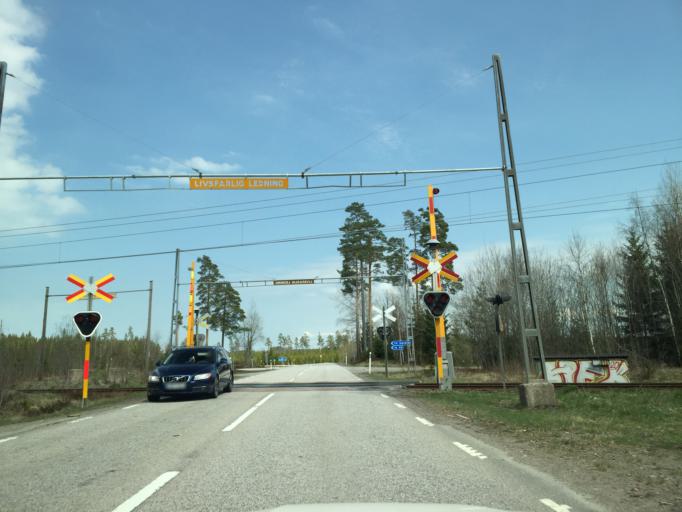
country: SE
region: Vaestra Goetaland
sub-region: Bengtsfors Kommun
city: Dals Langed
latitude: 58.8250
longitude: 12.1381
